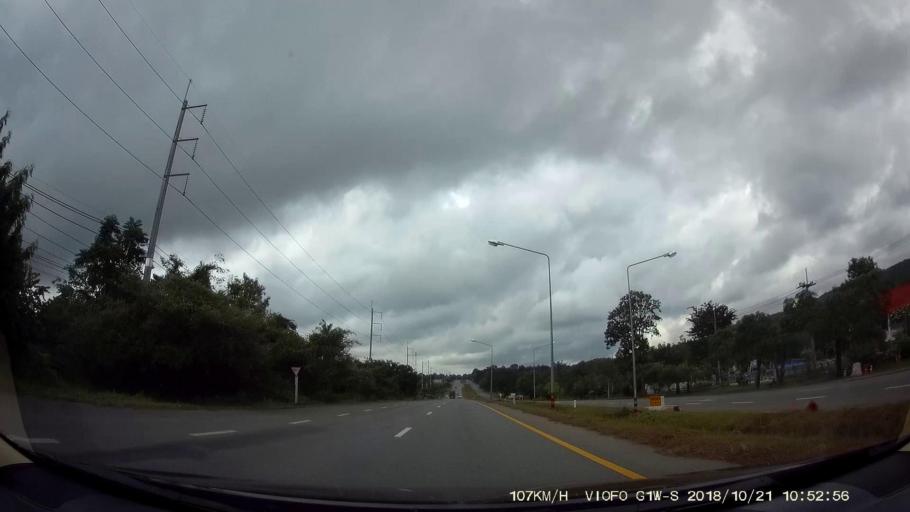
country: TH
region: Chaiyaphum
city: Khon Sawan
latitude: 15.9706
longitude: 102.1872
